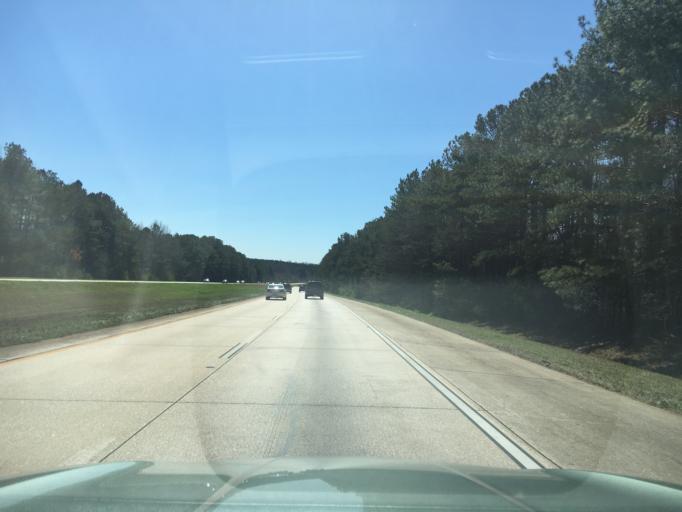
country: US
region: Georgia
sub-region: Troup County
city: Hogansville
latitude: 33.1064
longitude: -84.9064
